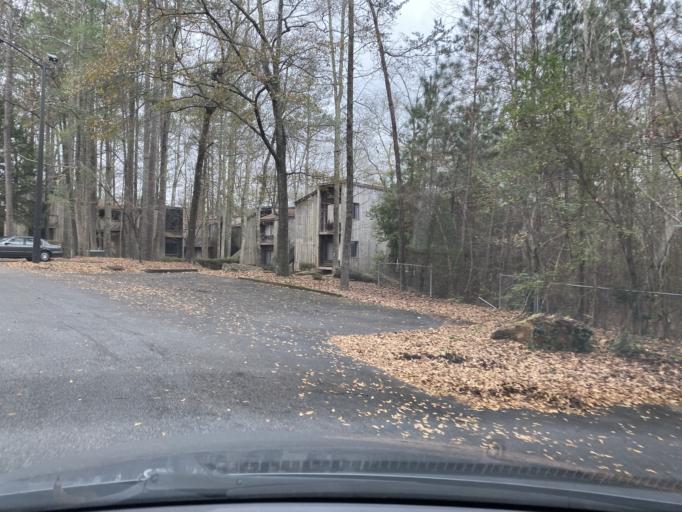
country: US
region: Georgia
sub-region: DeKalb County
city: Pine Mountain
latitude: 33.6948
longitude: -84.1480
